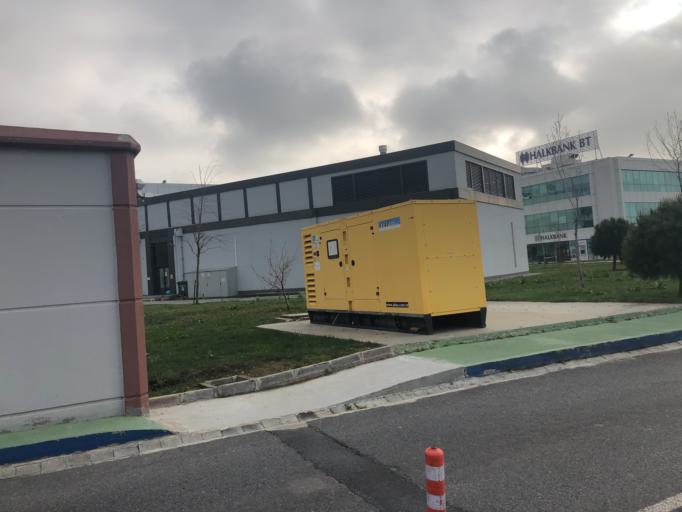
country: TR
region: Istanbul
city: merter keresteciler
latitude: 41.0201
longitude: 28.8877
